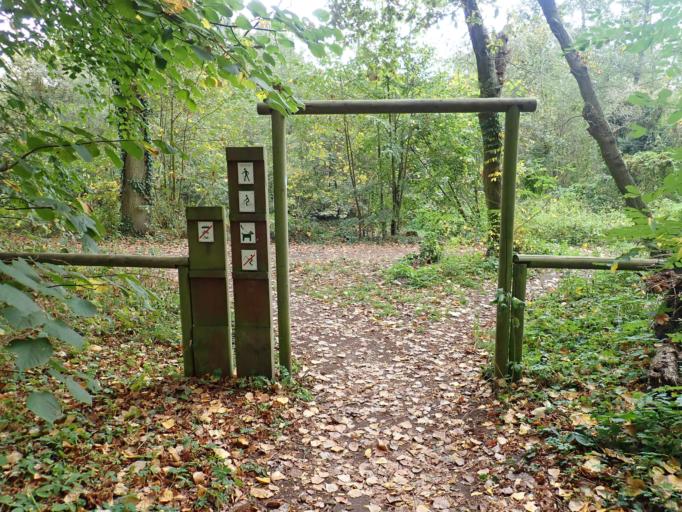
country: BE
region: Flanders
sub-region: Provincie Antwerpen
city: Willebroek
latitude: 51.0555
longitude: 4.3882
